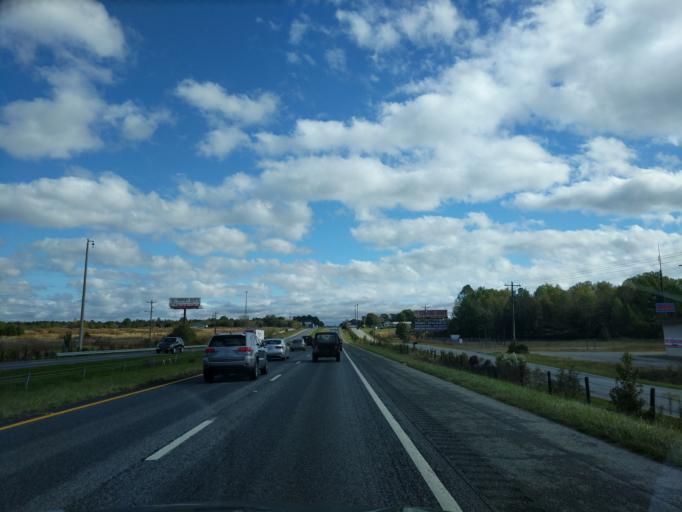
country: US
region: South Carolina
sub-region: Spartanburg County
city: Cowpens
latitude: 35.0606
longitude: -81.7790
